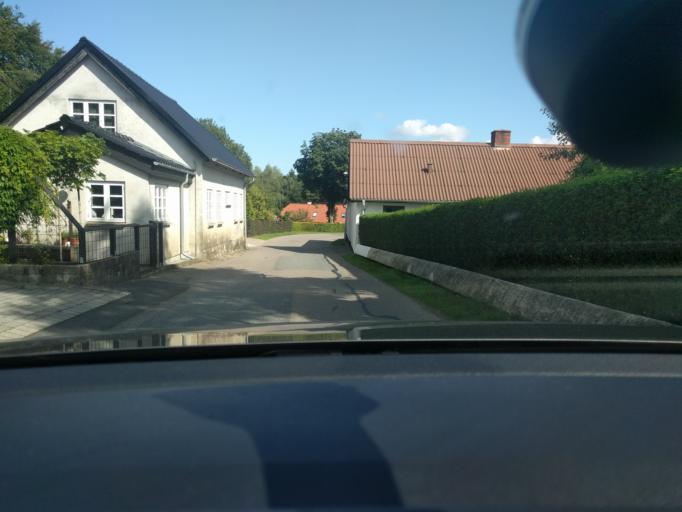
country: DK
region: Central Jutland
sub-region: Viborg Kommune
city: Viborg
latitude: 56.5108
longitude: 9.3067
